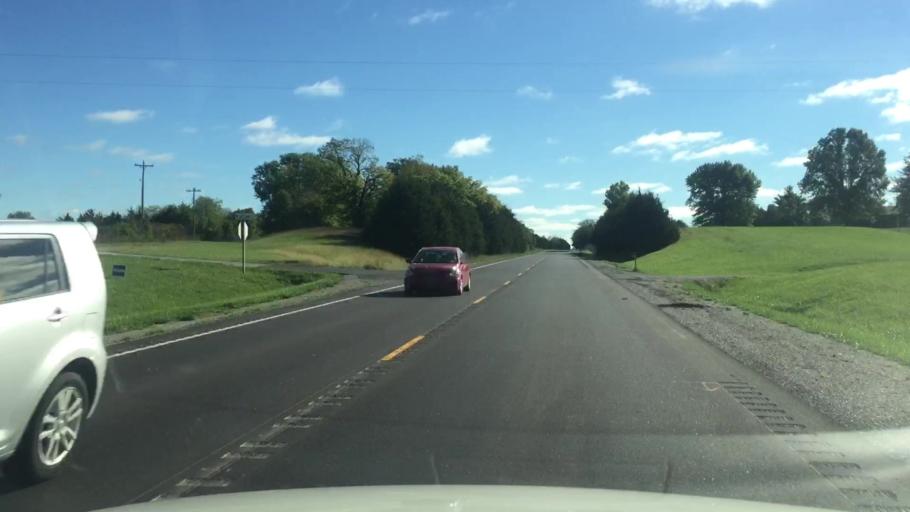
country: US
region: Missouri
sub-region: Boone County
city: Columbia
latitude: 38.9898
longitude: -92.5159
